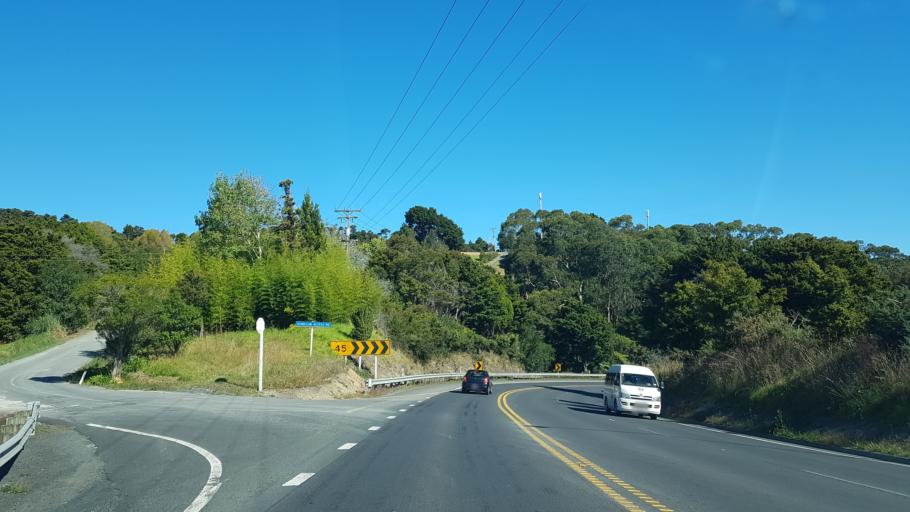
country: NZ
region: Auckland
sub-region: Auckland
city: Warkworth
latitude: -36.4799
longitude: 174.6576
